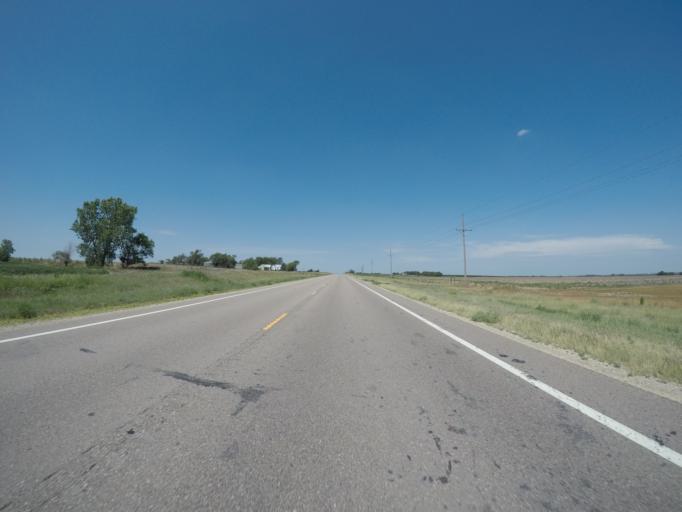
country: US
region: Kansas
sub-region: Osborne County
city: Osborne
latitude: 39.5099
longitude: -98.6460
